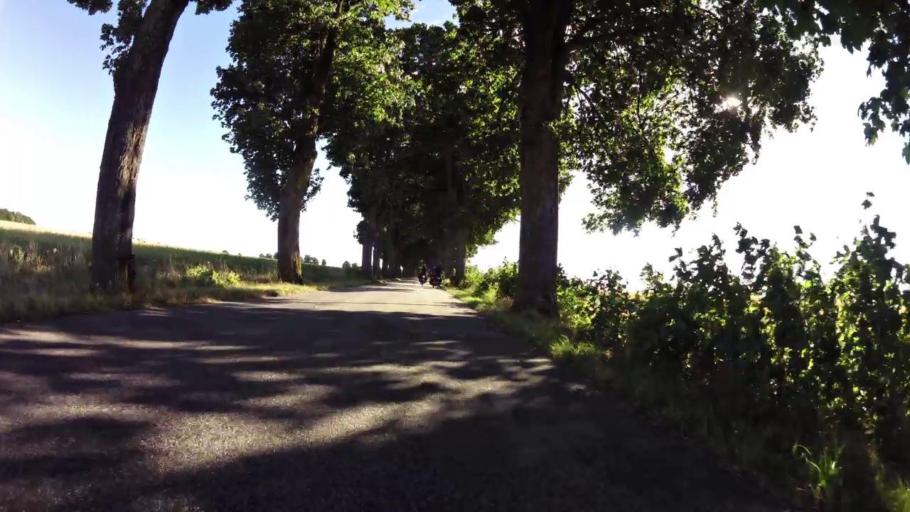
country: PL
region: West Pomeranian Voivodeship
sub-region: Powiat swidwinski
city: Swidwin
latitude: 53.7661
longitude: 15.7138
